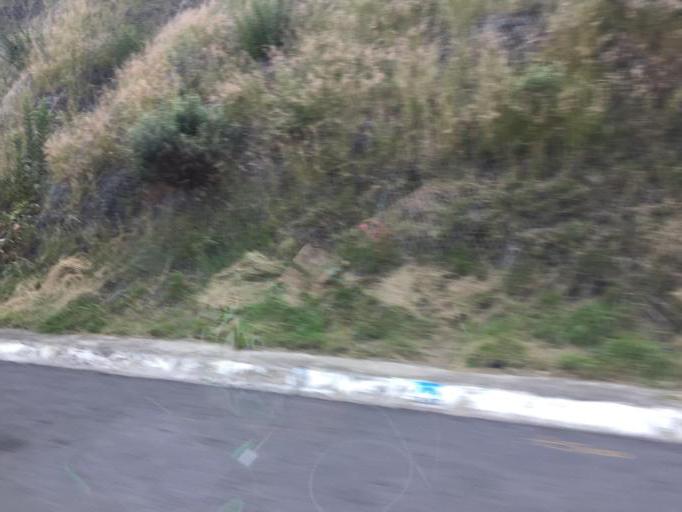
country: MX
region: Jalisco
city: Ocotlan
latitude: 20.4029
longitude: -102.7362
